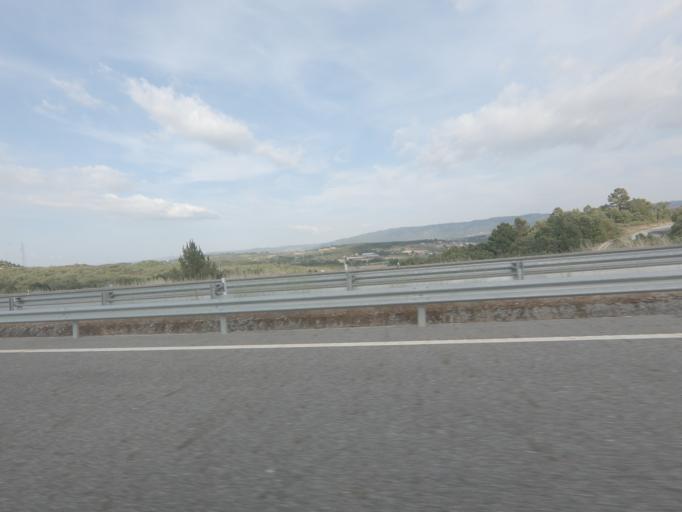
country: PT
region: Vila Real
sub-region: Chaves
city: Chaves
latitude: 41.7236
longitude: -7.5425
